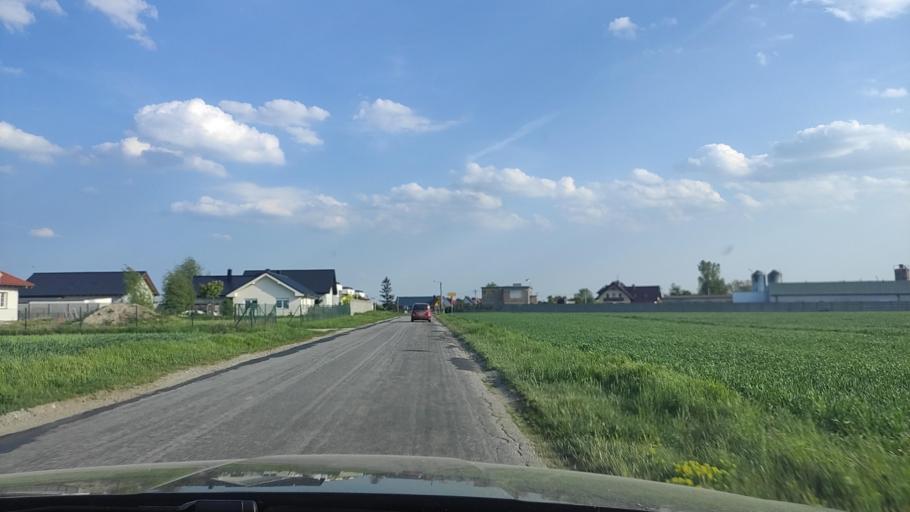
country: PL
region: Greater Poland Voivodeship
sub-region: Powiat poznanski
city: Kleszczewo
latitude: 52.3590
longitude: 17.1712
